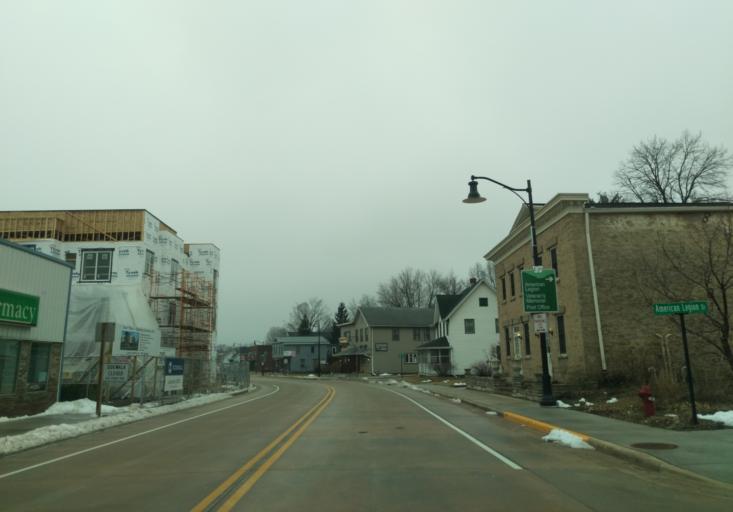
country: US
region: Wisconsin
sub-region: Dane County
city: Cross Plains
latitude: 43.1136
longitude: -89.6497
